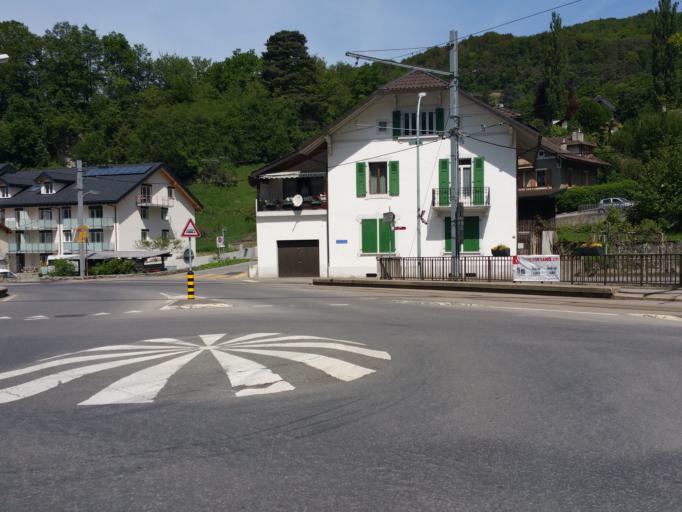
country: CH
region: Vaud
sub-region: Aigle District
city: Bex
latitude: 46.2504
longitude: 7.0205
